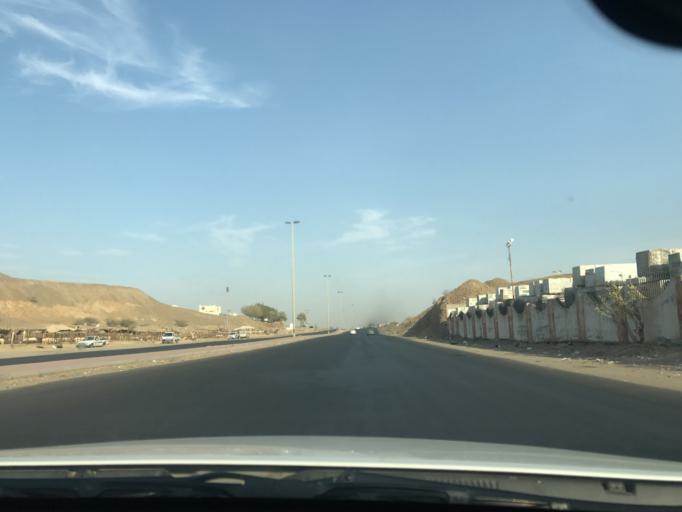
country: SA
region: Makkah
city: Jeddah
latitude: 21.4148
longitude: 39.4156
